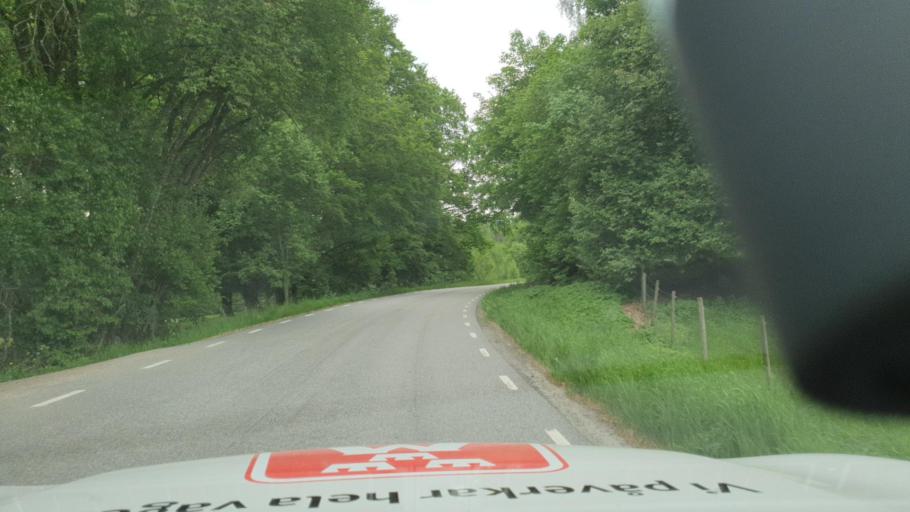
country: SE
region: Vaestra Goetaland
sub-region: Ulricehamns Kommun
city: Ulricehamn
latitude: 57.8538
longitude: 13.2846
